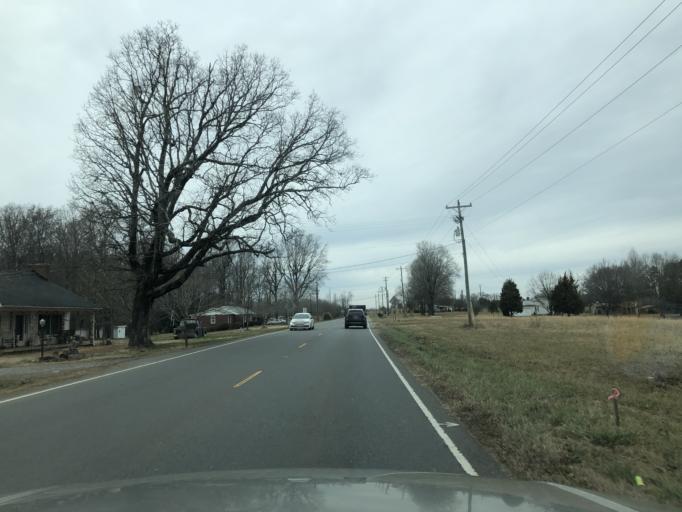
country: US
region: North Carolina
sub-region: Cleveland County
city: Shelby
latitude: 35.3072
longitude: -81.4874
